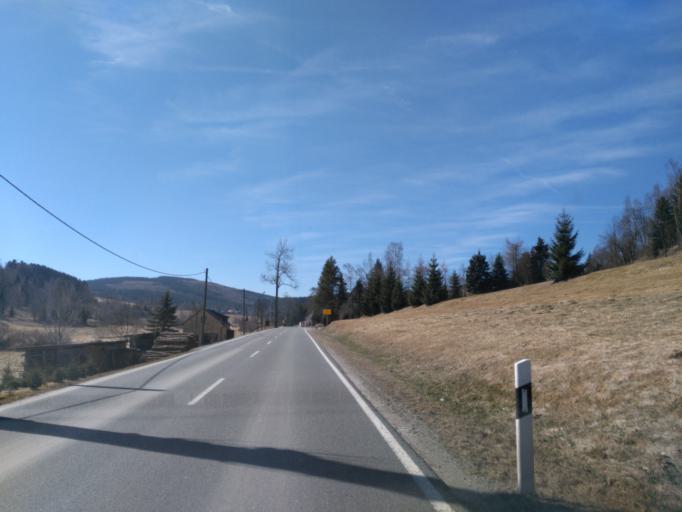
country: CZ
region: Ustecky
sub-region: Okres Chomutov
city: Kovarska
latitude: 50.4506
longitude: 13.0212
